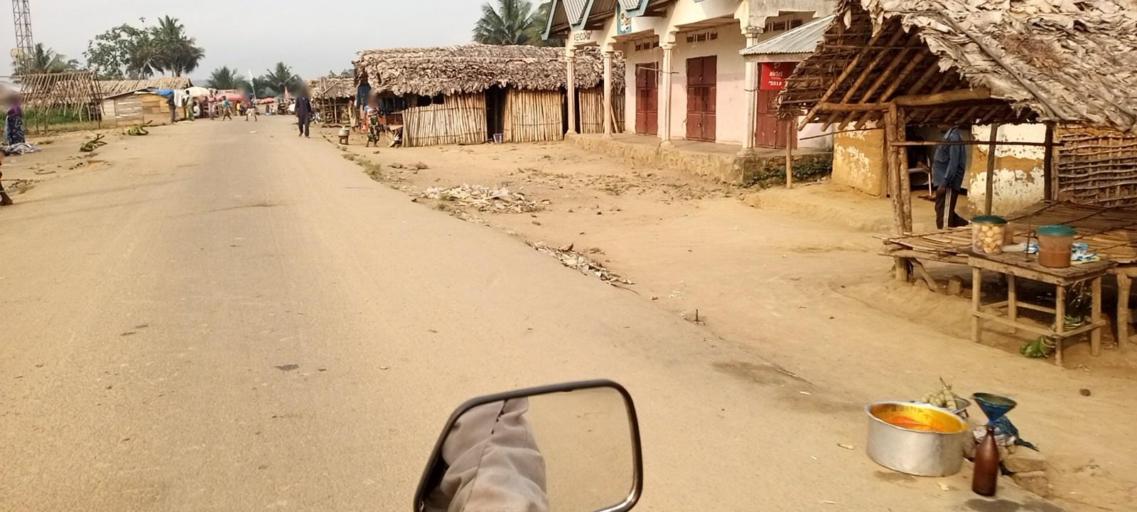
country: CD
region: Eastern Province
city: Kisangani
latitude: 0.1938
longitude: 25.5290
